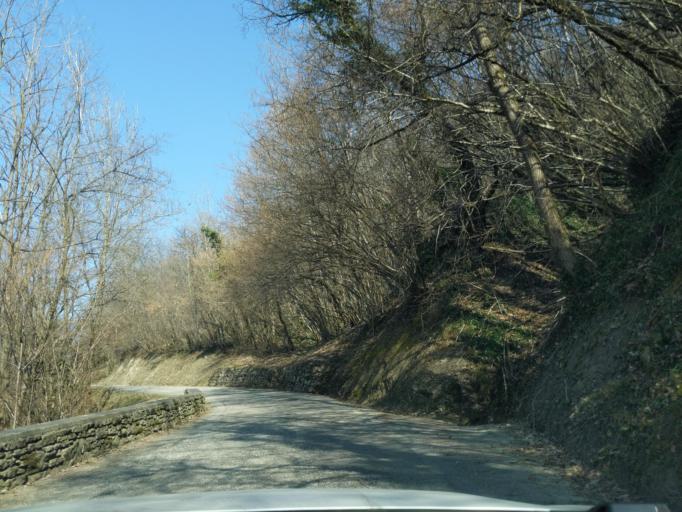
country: FR
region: Rhone-Alpes
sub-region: Departement de la Savoie
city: Chindrieux
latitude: 45.8875
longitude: 5.8482
